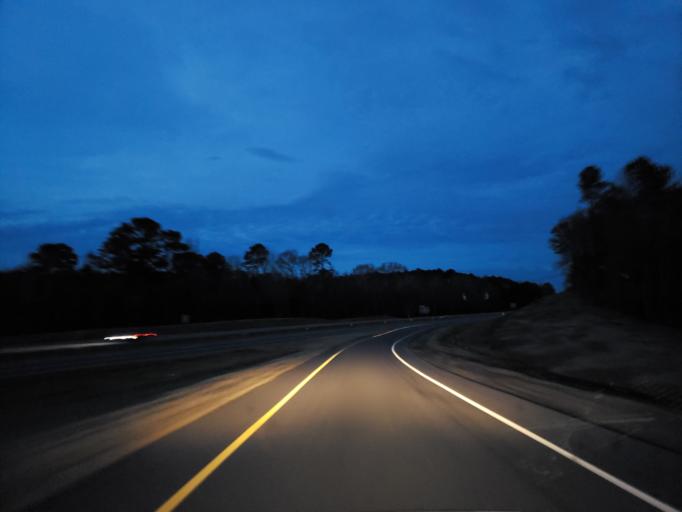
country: US
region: Alabama
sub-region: Greene County
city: Eutaw
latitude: 32.8691
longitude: -87.9225
